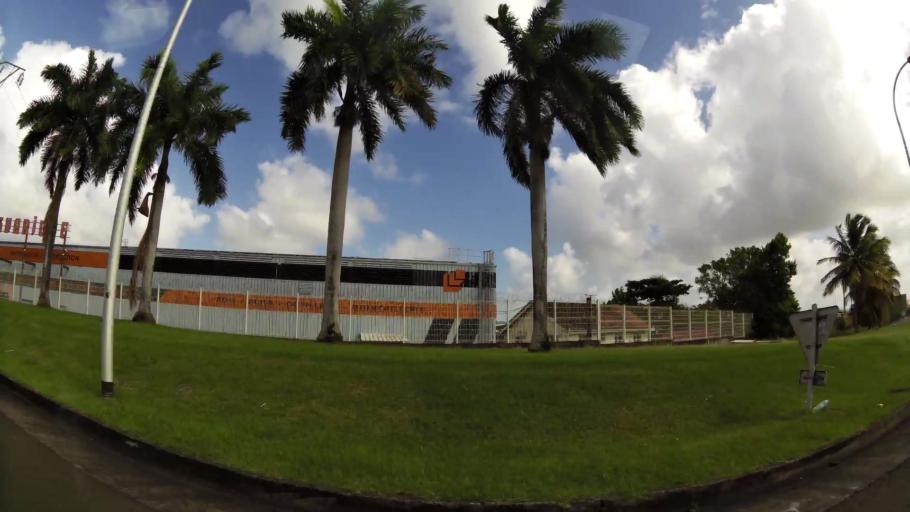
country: MQ
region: Martinique
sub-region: Martinique
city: Le Lamentin
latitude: 14.6232
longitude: -60.9887
